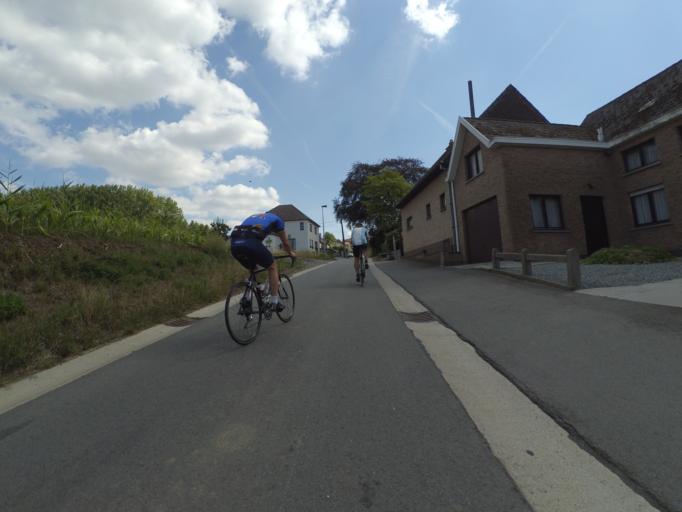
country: BE
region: Flanders
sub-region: Provincie Oost-Vlaanderen
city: Zottegem
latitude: 50.8339
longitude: 3.7729
